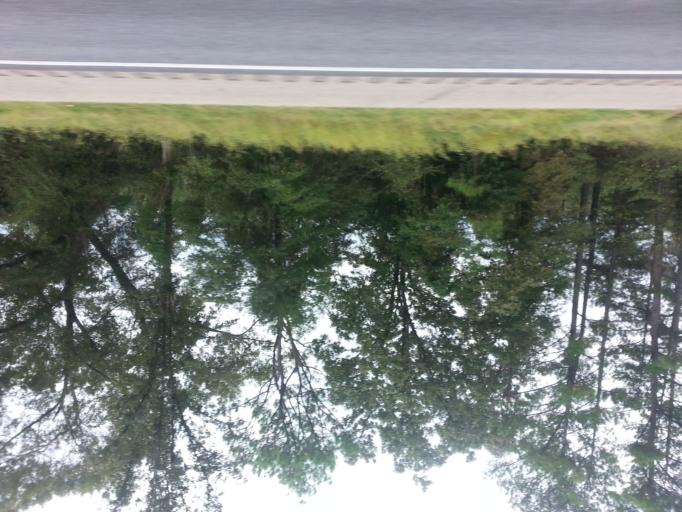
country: US
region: Alabama
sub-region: Escambia County
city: Brewton
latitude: 31.2809
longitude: -87.1990
